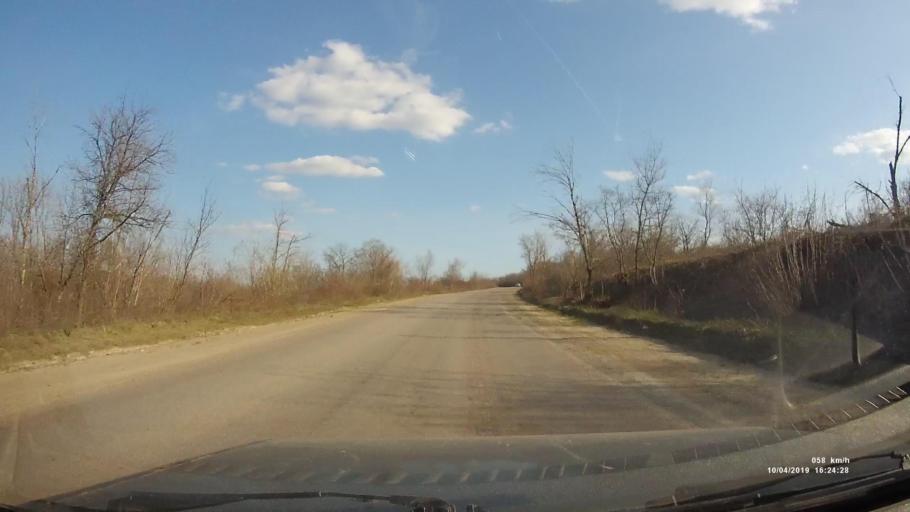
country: RU
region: Rostov
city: Staraya Stanitsa
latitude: 48.2995
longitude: 40.3151
